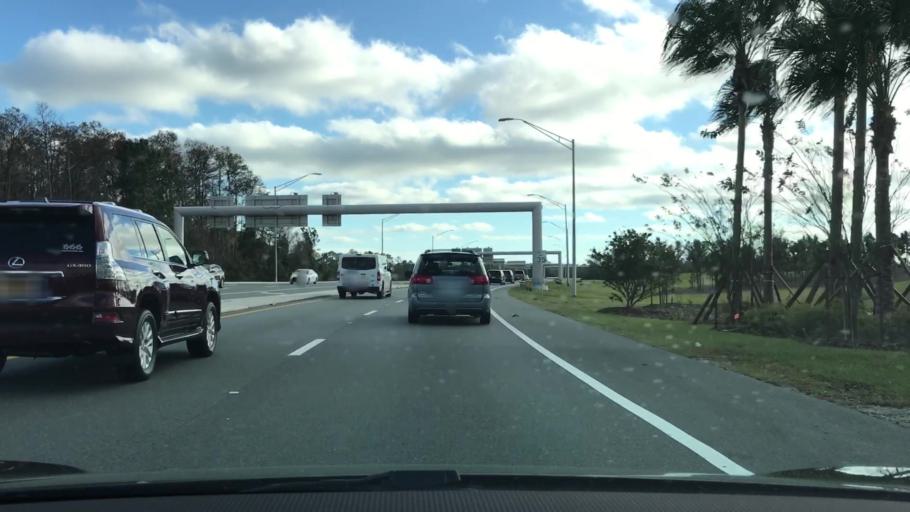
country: US
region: Florida
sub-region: Orange County
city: Taft
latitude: 28.4148
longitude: -81.3042
